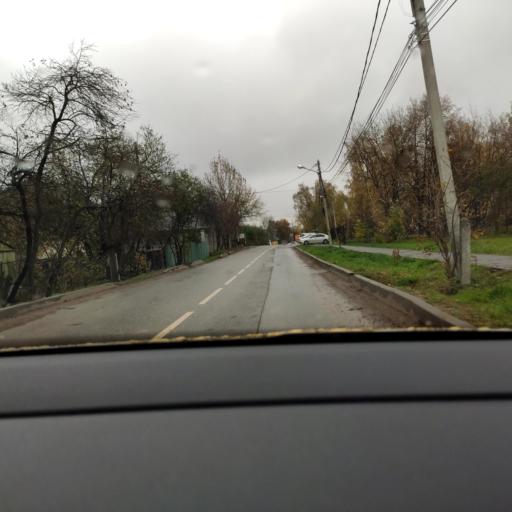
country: RU
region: Moskovskaya
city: Shcherbinka
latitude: 55.4996
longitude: 37.5423
